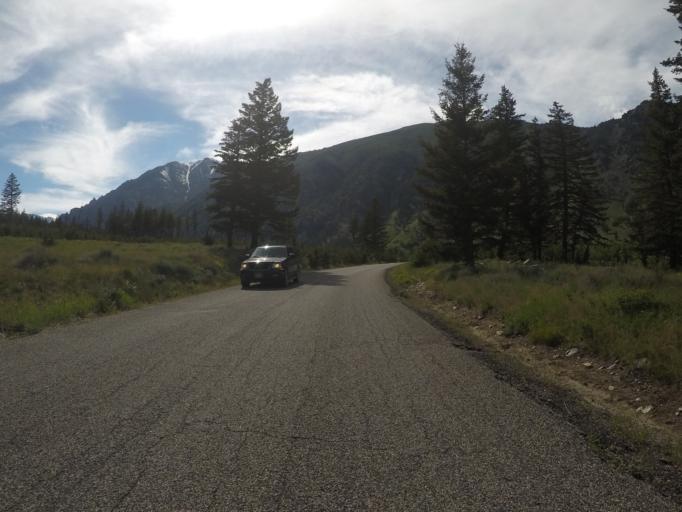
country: US
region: Montana
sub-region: Stillwater County
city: Absarokee
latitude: 45.2463
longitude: -109.5798
